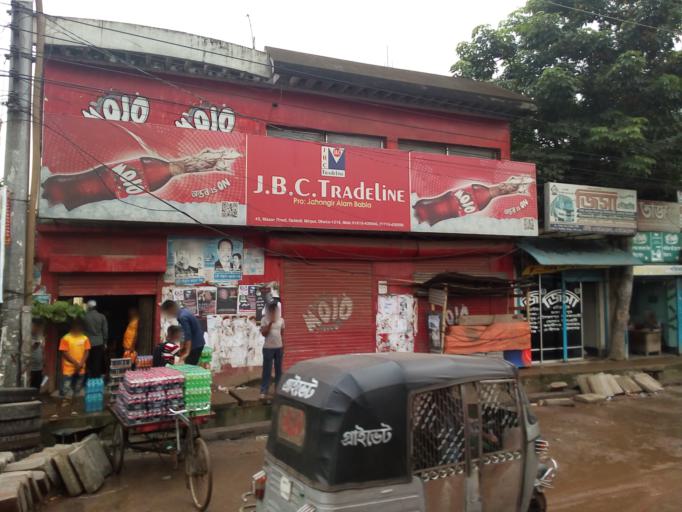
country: BD
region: Dhaka
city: Azimpur
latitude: 23.7830
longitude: 90.3480
